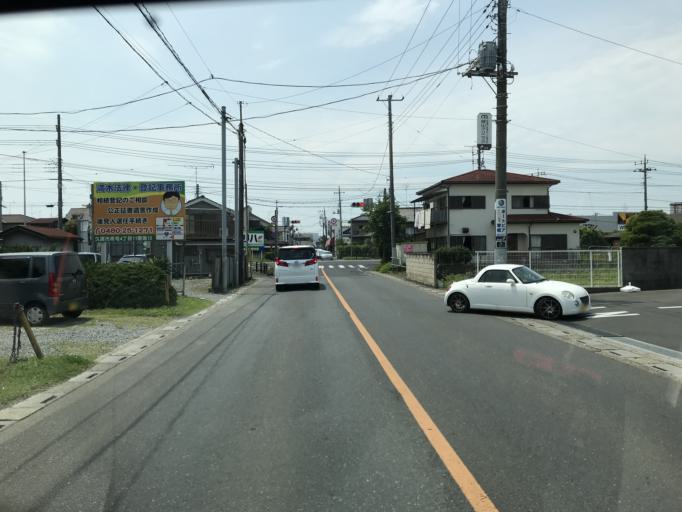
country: JP
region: Saitama
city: Satte
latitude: 36.0792
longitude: 139.7250
